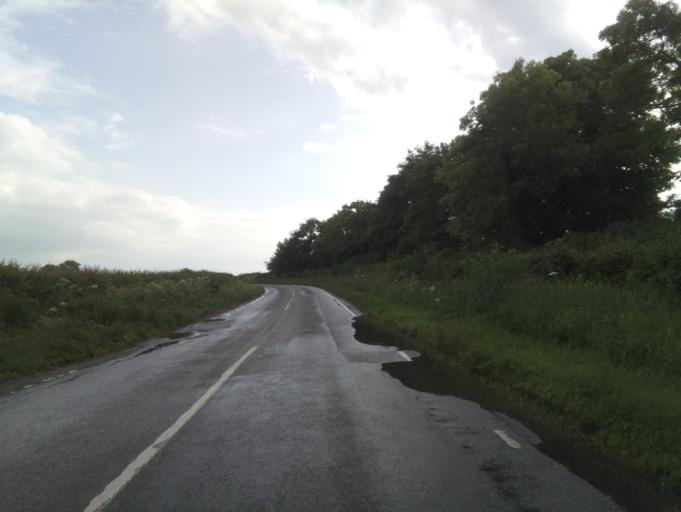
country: GB
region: England
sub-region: Lincolnshire
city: Great Gonerby
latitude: 53.0168
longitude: -0.6602
